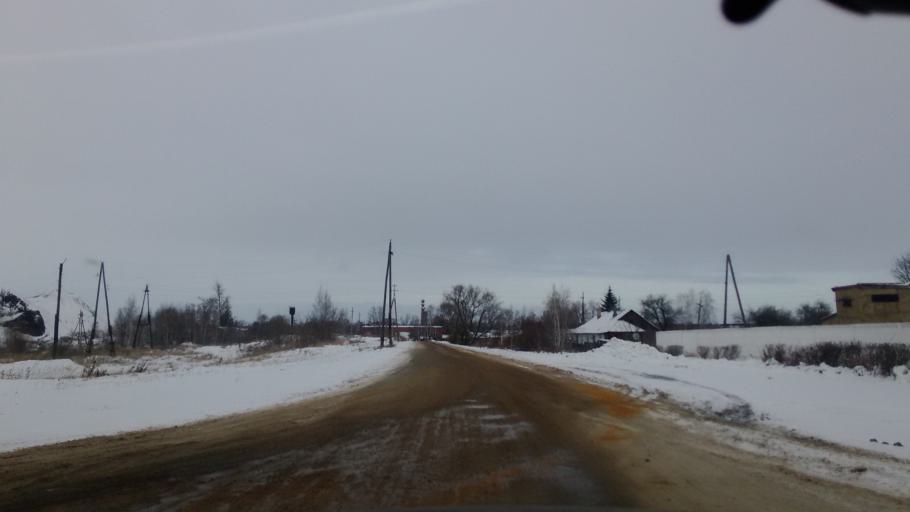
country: RU
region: Tula
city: Bogoroditsk
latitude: 53.7577
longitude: 38.1065
